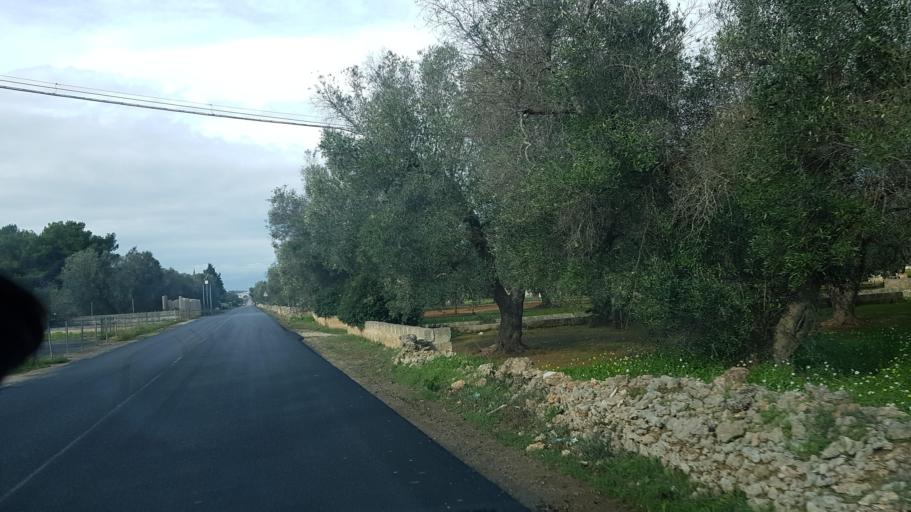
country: IT
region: Apulia
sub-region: Provincia di Brindisi
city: Oria
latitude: 40.4837
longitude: 17.6798
